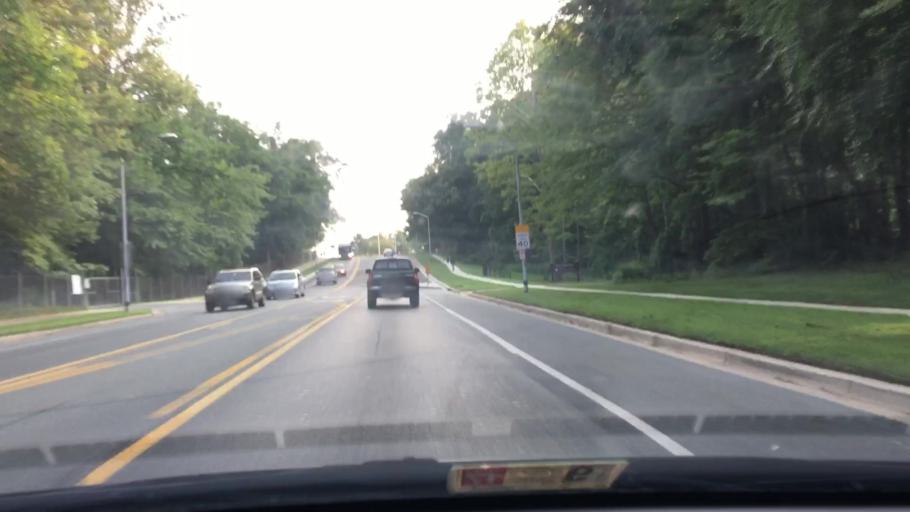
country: US
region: Maryland
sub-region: Montgomery County
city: Aspen Hill
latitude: 39.0887
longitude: -77.0725
